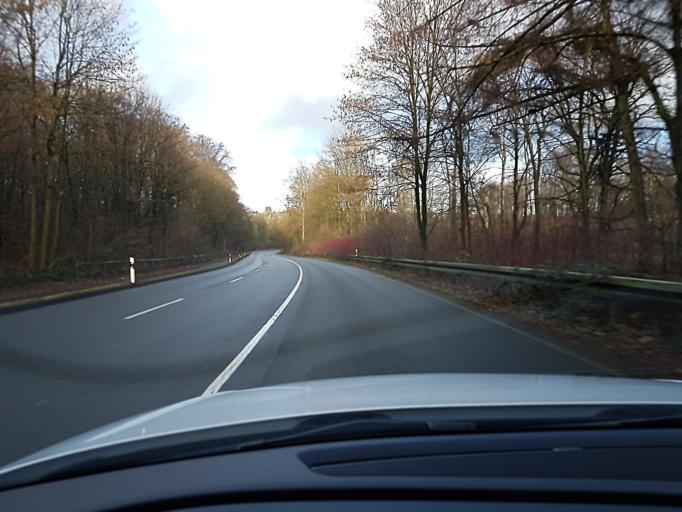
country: DE
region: North Rhine-Westphalia
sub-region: Regierungsbezirk Dusseldorf
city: Muelheim (Ruhr)
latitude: 51.4208
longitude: 6.9025
